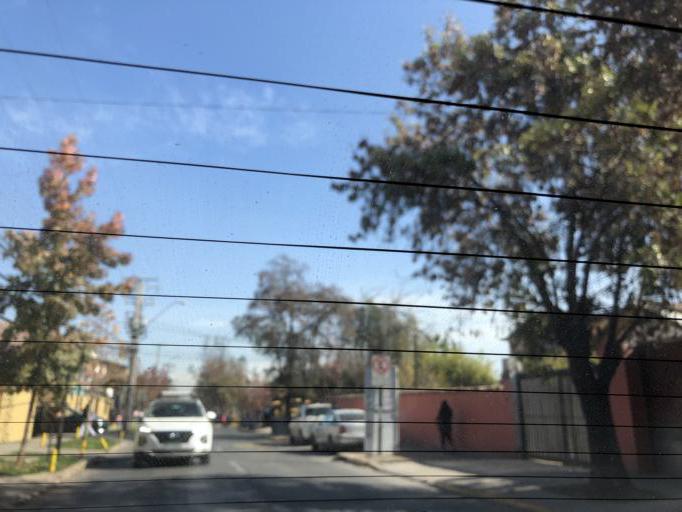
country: CL
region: Santiago Metropolitan
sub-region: Provincia de Cordillera
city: Puente Alto
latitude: -33.6009
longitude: -70.5807
